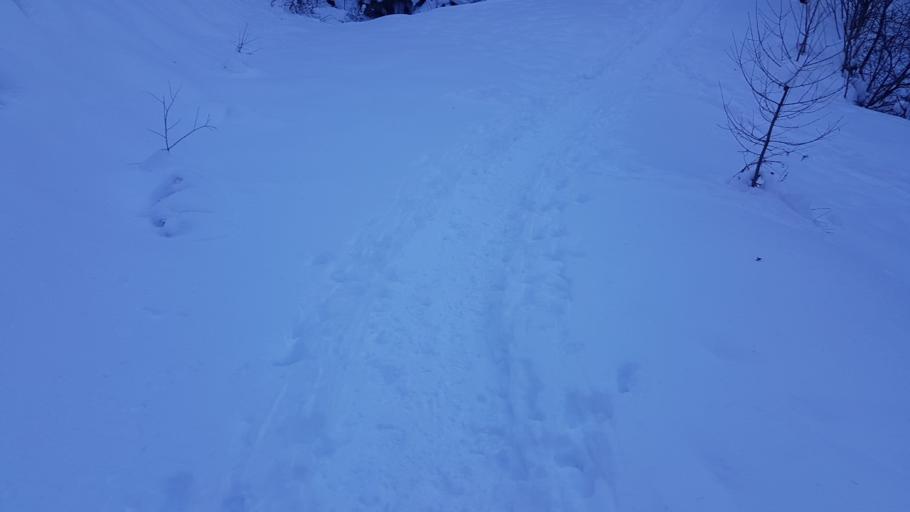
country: IT
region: Piedmont
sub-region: Provincia di Torino
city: Cesana Torinese
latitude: 44.9808
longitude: 6.8129
